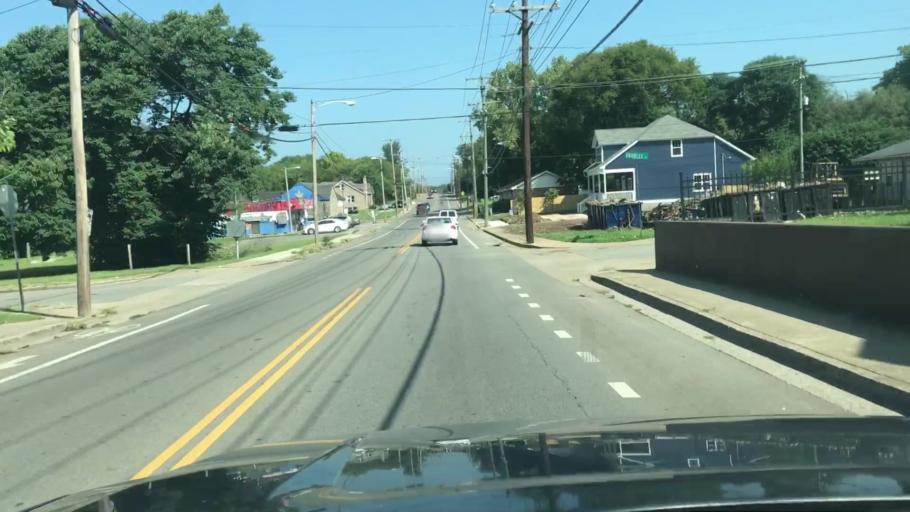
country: US
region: Tennessee
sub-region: Davidson County
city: Nashville
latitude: 36.1721
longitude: -86.8077
